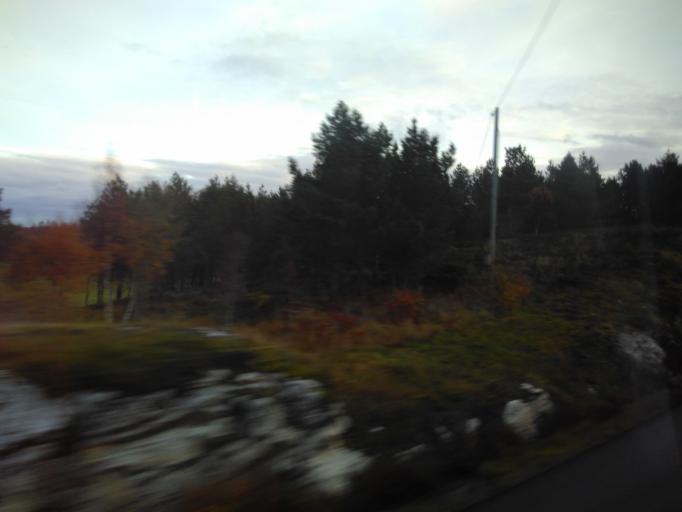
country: NO
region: Sor-Trondelag
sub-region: Froya
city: Sistranda
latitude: 63.6351
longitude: 8.8331
